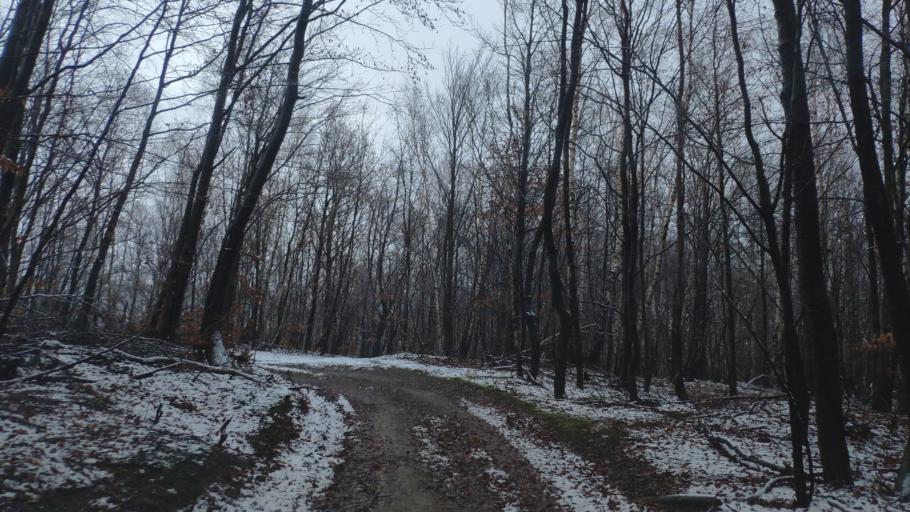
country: SK
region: Kosicky
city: Moldava nad Bodvou
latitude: 48.7377
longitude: 21.0771
